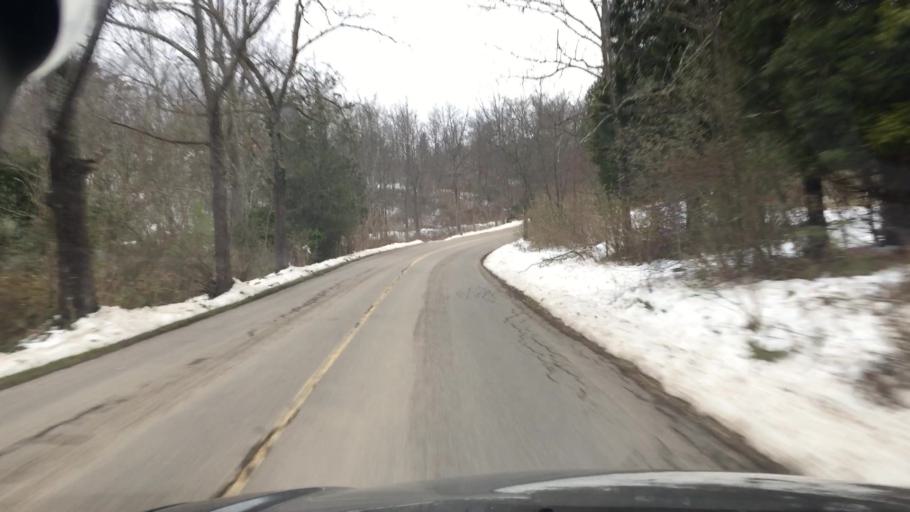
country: US
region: Pennsylvania
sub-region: Luzerne County
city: Conyngham
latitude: 41.0032
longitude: -76.1375
